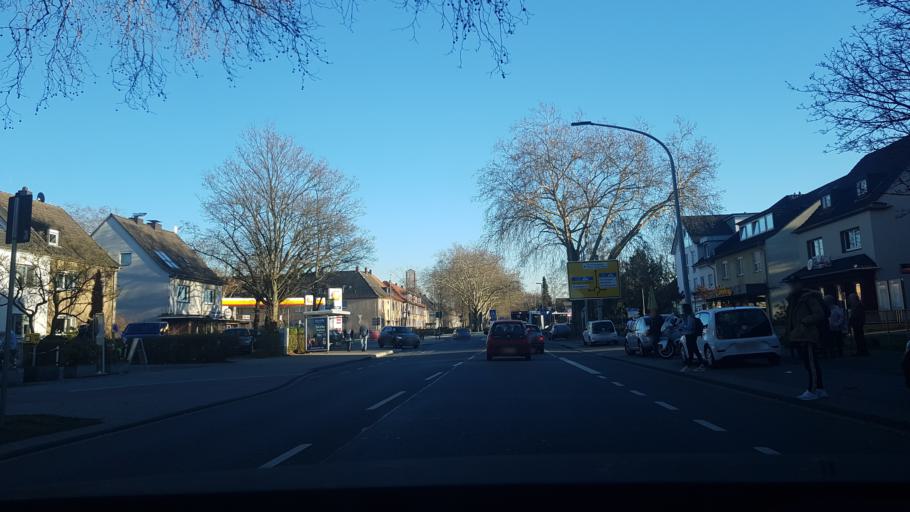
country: DE
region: North Rhine-Westphalia
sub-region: Regierungsbezirk Dusseldorf
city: Hochfeld
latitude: 51.3932
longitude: 6.7905
